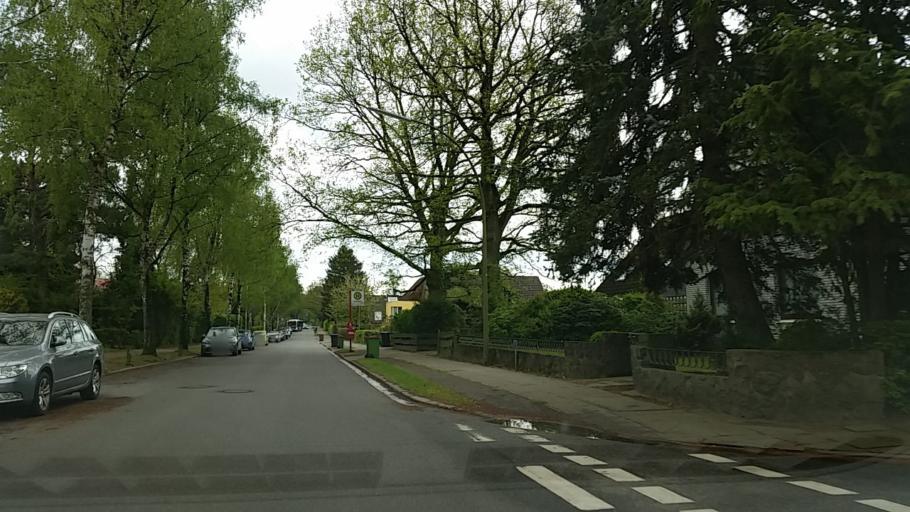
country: DE
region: Hamburg
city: Sasel
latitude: 53.6613
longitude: 10.1070
